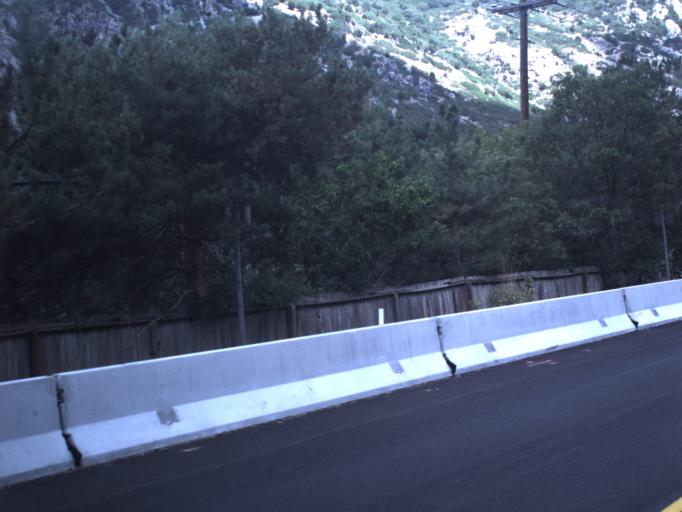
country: US
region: Utah
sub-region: Salt Lake County
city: Granite
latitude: 40.5735
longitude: -111.7869
